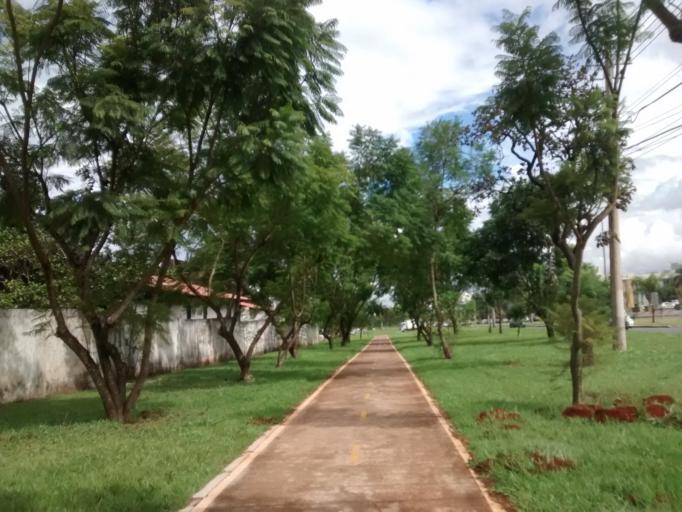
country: BR
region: Federal District
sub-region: Brasilia
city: Brasilia
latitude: -15.7926
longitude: -47.9162
